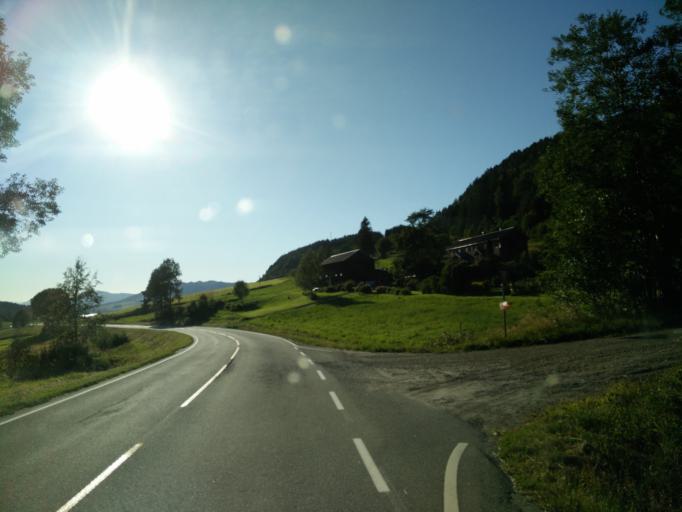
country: NO
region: More og Romsdal
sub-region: Halsa
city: Liaboen
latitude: 63.0873
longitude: 8.3870
